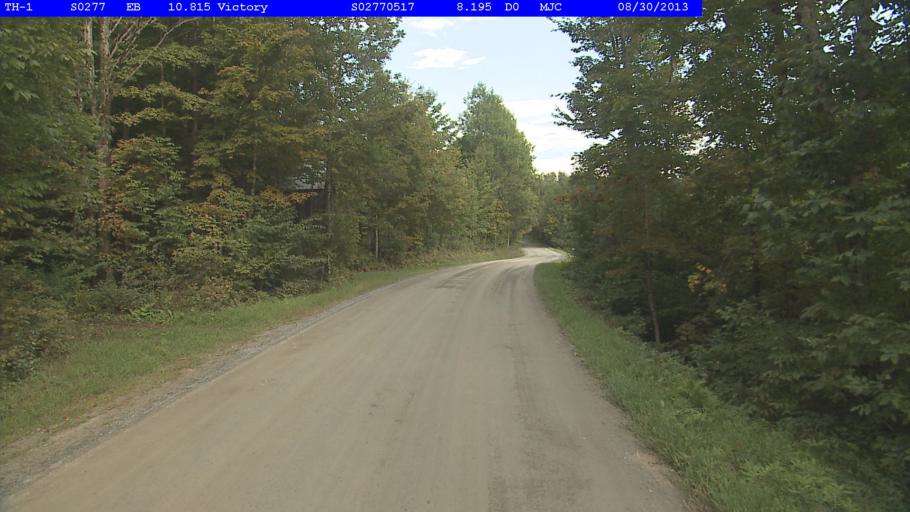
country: US
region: Vermont
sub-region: Essex County
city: Guildhall
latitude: 44.5708
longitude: -71.7714
